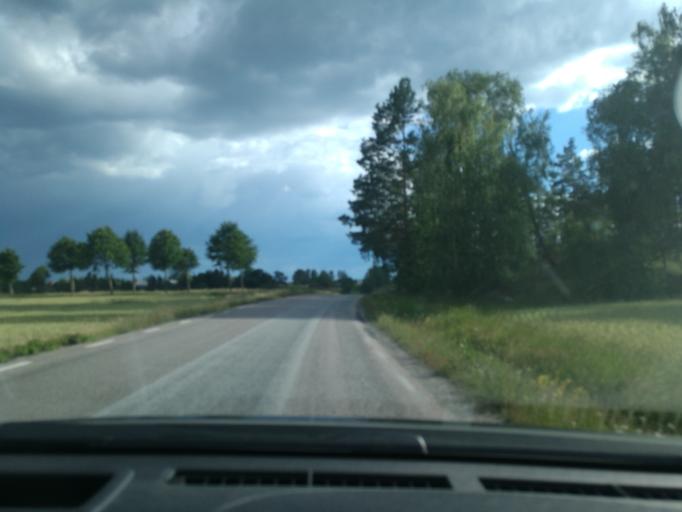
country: SE
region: Soedermanland
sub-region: Eskilstuna Kommun
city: Arla
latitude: 59.4014
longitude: 16.6797
